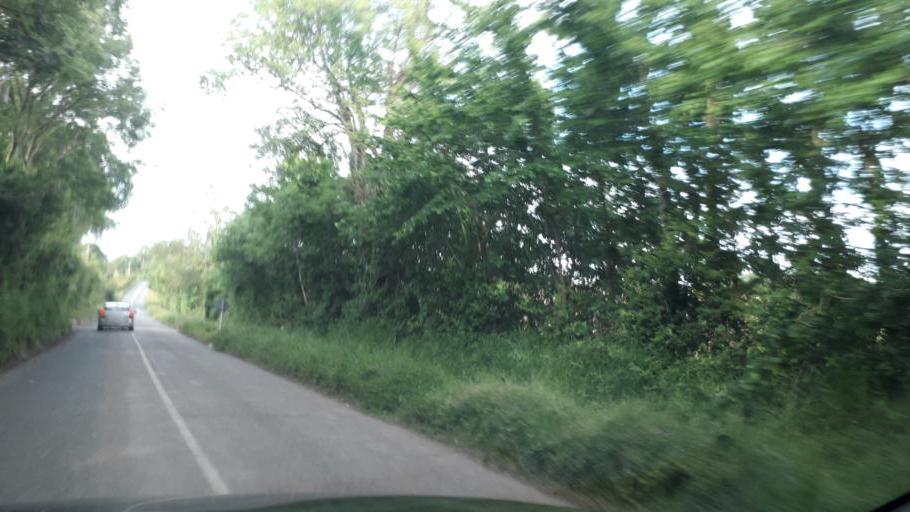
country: IE
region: Leinster
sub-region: Loch Garman
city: Courtown
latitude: 52.5477
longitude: -6.2523
